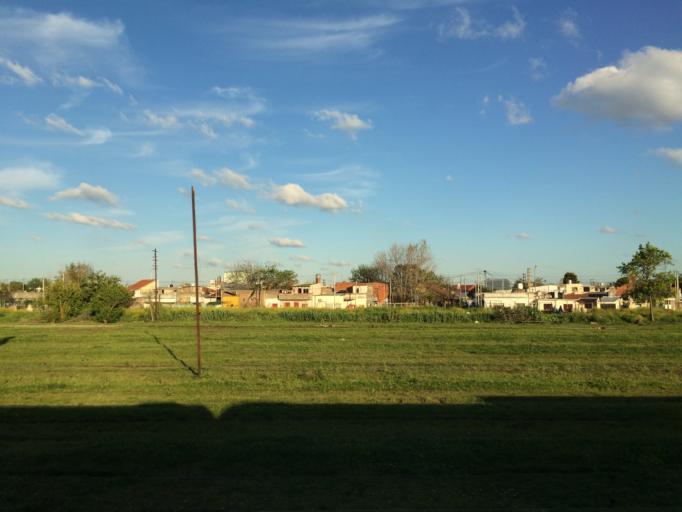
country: AR
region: Buenos Aires
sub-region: Partido de Lanus
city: Lanus
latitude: -34.6899
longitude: -58.3840
